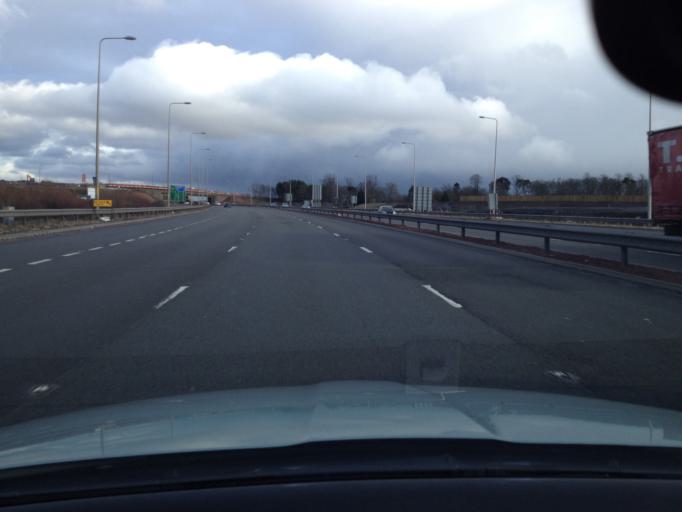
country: GB
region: Scotland
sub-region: Edinburgh
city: Queensferry
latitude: 55.9819
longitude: -3.4014
